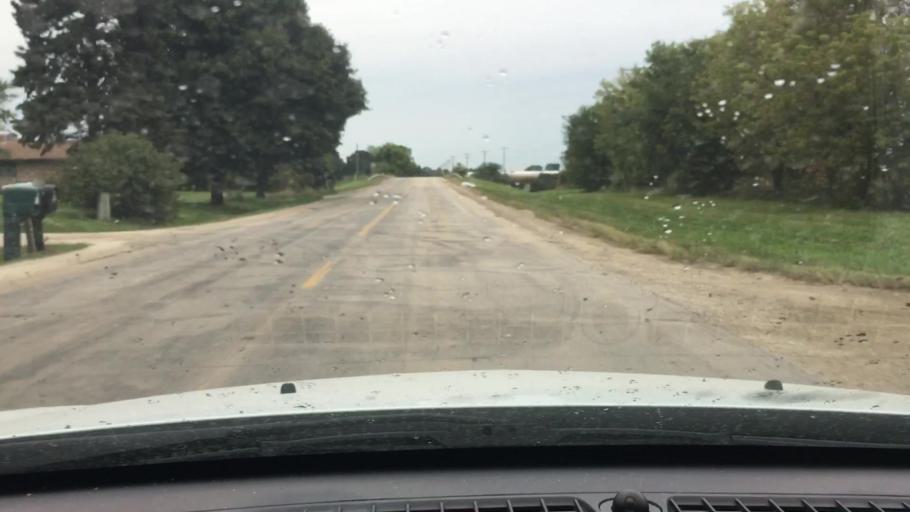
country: US
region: Illinois
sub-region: Ogle County
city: Rochelle
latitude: 41.8988
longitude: -89.0537
